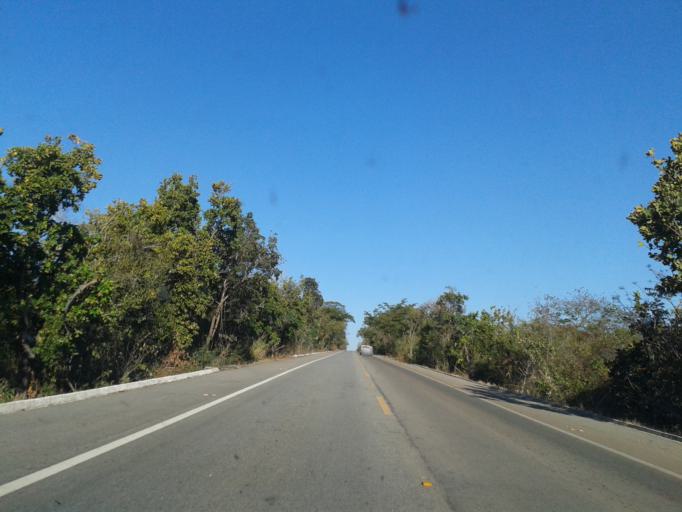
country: BR
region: Goias
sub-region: Itapirapua
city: Itapirapua
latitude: -15.3224
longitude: -50.4344
